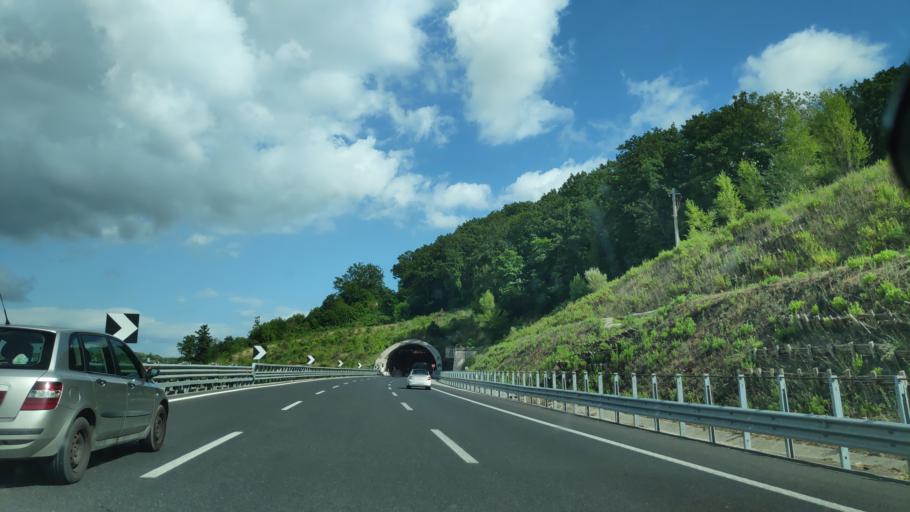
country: IT
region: Campania
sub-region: Provincia di Salerno
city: Contursi Terme
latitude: 40.6273
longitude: 15.2357
